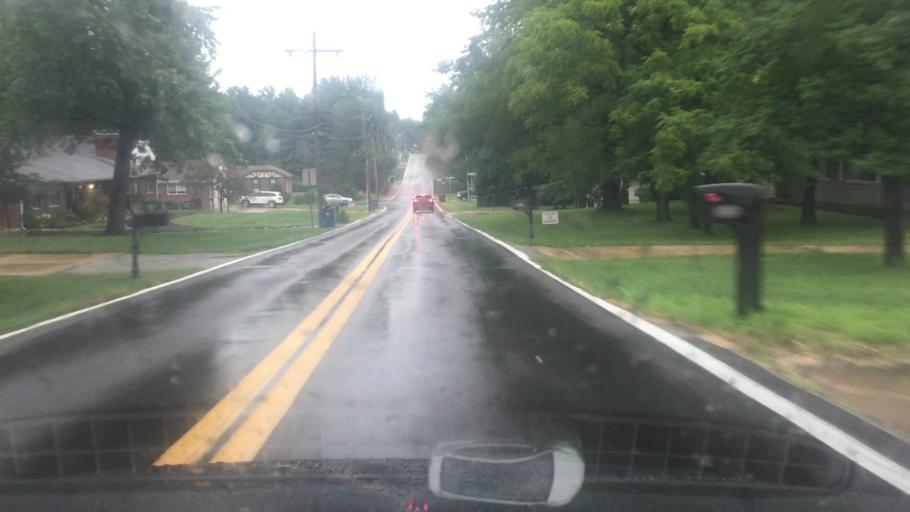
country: US
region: Missouri
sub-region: Saint Louis County
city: Concord
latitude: 38.5139
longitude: -90.3600
